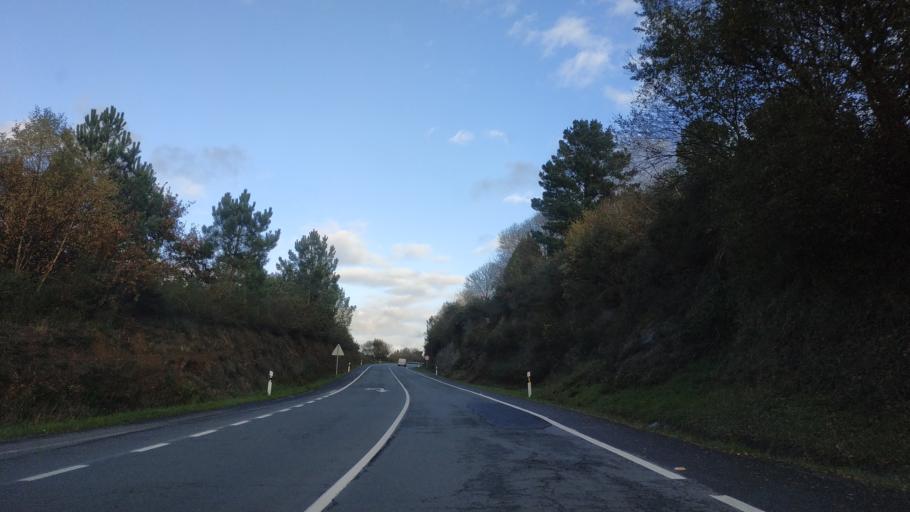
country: ES
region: Galicia
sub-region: Provincia de Pontevedra
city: Silleda
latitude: 42.7952
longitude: -8.1680
